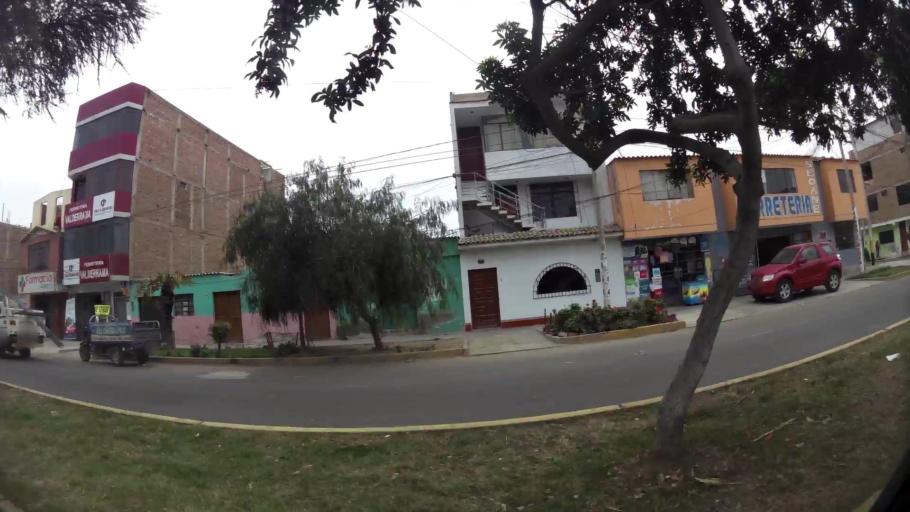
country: PE
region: La Libertad
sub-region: Provincia de Trujillo
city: Buenos Aires
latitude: -8.1384
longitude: -79.0450
